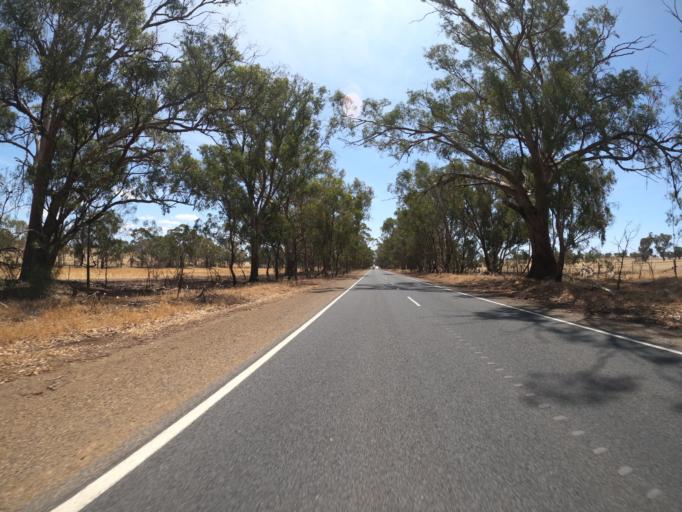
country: AU
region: Victoria
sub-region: Benalla
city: Benalla
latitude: -36.3685
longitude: 145.9712
